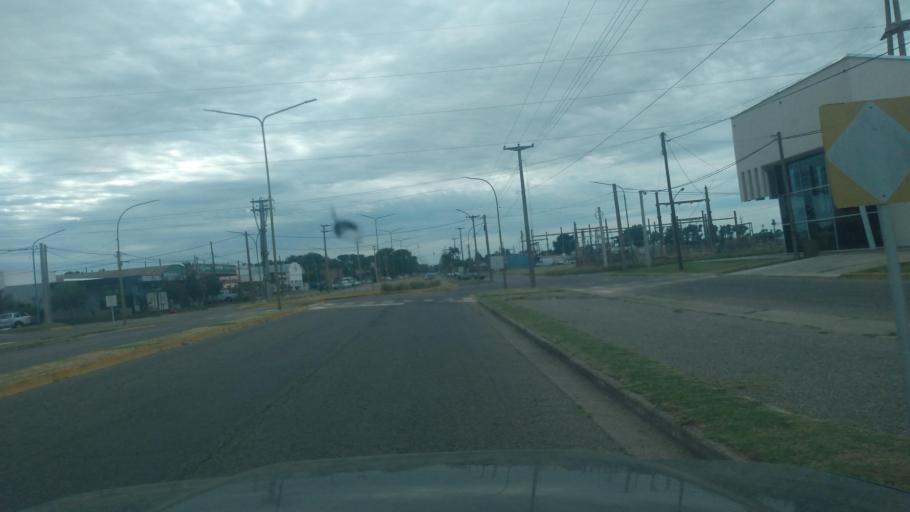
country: AR
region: Buenos Aires
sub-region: Partido de Trenque Lauquen
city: Trenque Lauquen
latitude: -35.9842
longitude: -62.7253
